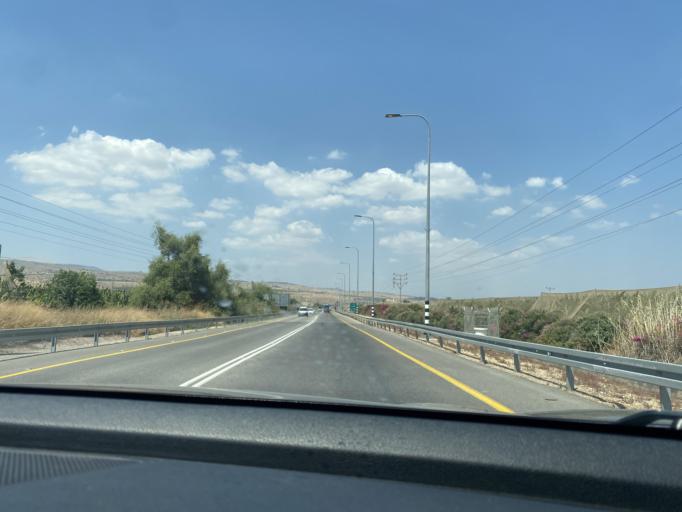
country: IL
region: Northern District
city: Tiberias
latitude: 32.8462
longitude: 35.5169
